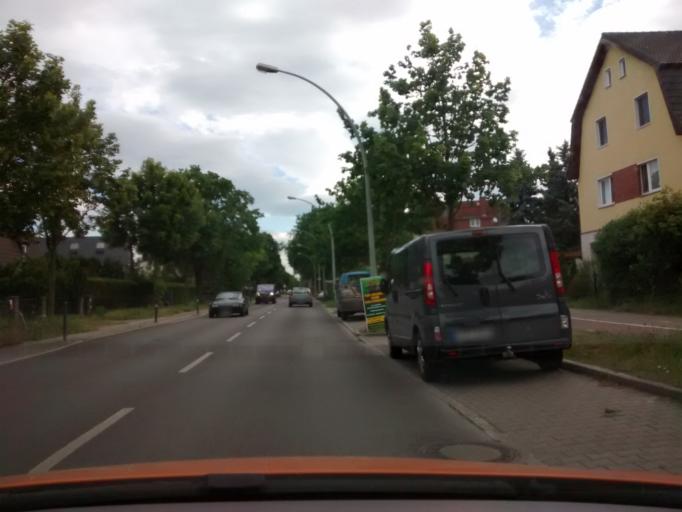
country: DE
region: Berlin
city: Bohnsdorf
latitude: 52.3941
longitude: 13.5732
